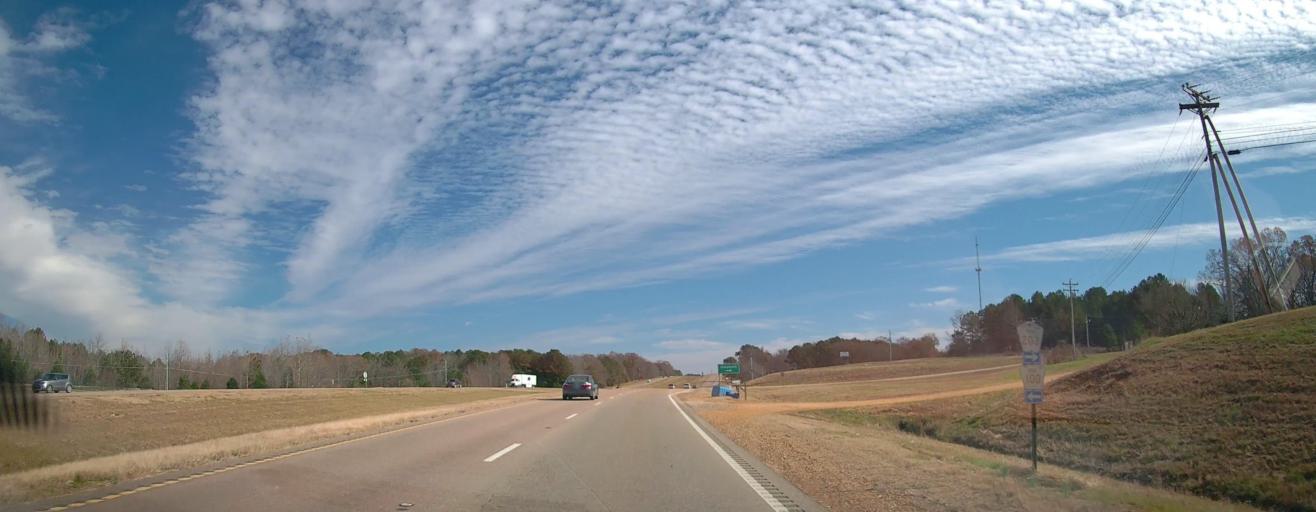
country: US
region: Mississippi
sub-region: Tippah County
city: Ripley
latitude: 34.9555
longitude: -88.8513
